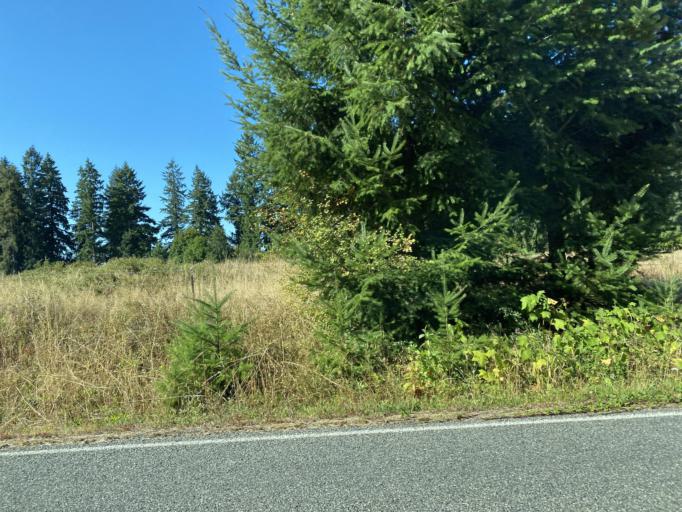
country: US
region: Washington
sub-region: Thurston County
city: Rainier
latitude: 46.8993
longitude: -122.7554
